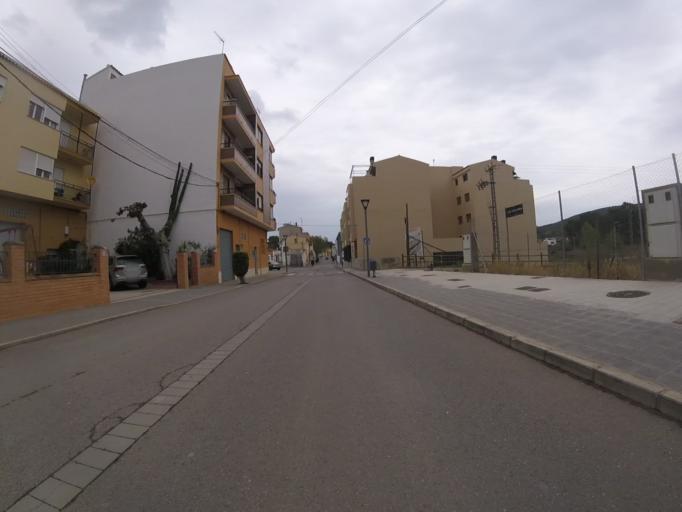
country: ES
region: Valencia
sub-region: Provincia de Castello
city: Cuevas de Vinroma
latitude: 40.3128
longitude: 0.1215
